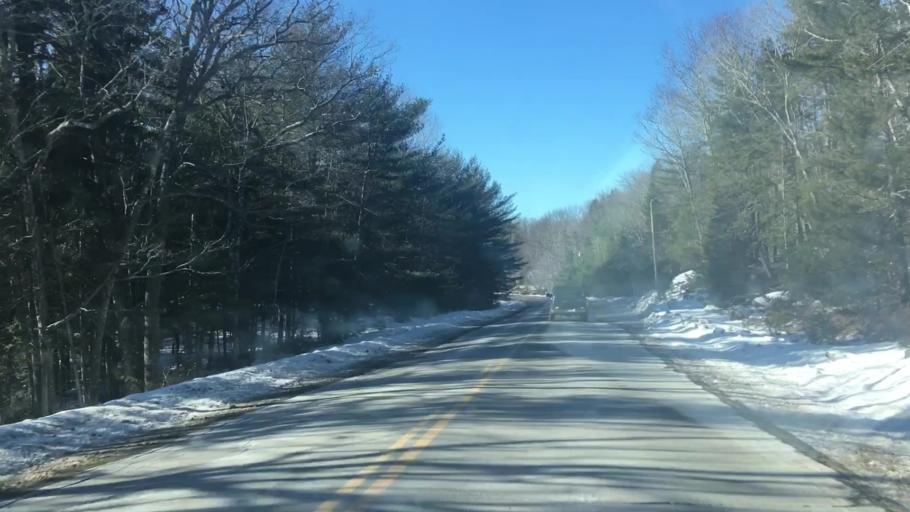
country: US
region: Maine
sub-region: Hancock County
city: Sedgwick
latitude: 44.3978
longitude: -68.6303
